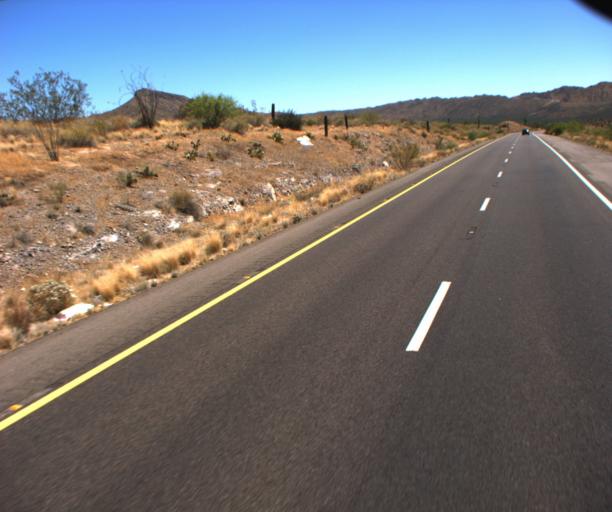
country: US
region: Arizona
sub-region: Maricopa County
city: Rio Verde
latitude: 33.7442
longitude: -111.5040
